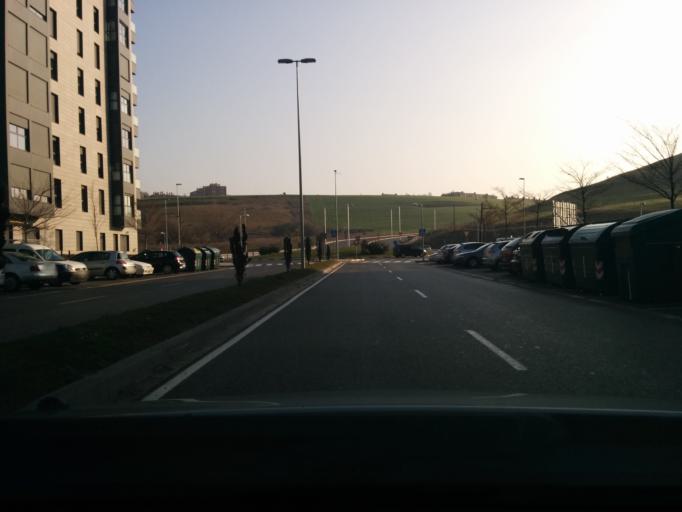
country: ES
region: Navarre
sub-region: Provincia de Navarra
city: Burlata
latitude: 42.8047
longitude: -1.6227
